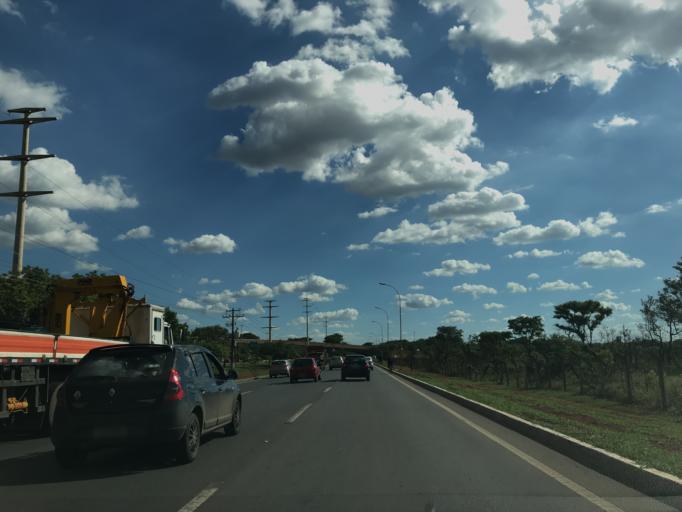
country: BR
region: Federal District
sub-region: Brasilia
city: Brasilia
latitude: -15.7821
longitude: -47.9410
